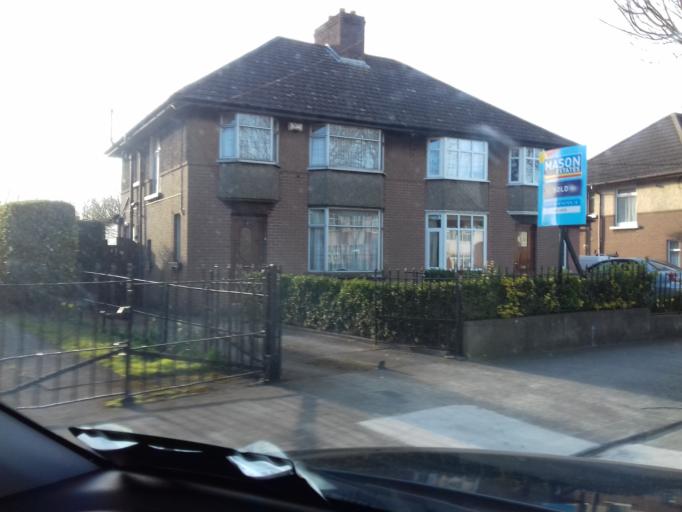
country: IE
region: Leinster
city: Cabra
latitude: 53.3602
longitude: -6.2922
